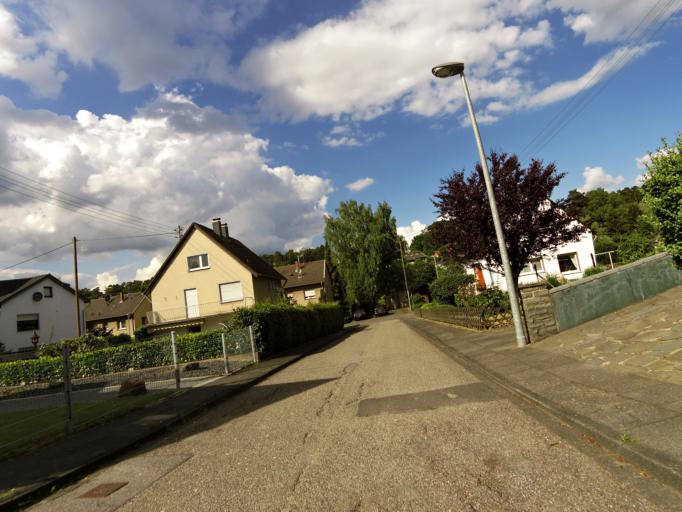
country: DE
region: North Rhine-Westphalia
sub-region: Regierungsbezirk Koln
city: Alfter
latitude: 50.6894
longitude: 7.0333
